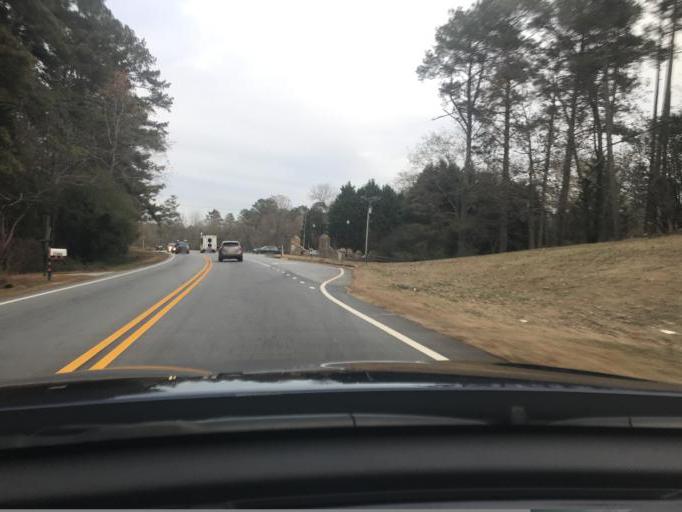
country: US
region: Georgia
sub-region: Newton County
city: Porterdale
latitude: 33.5797
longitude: -83.9265
